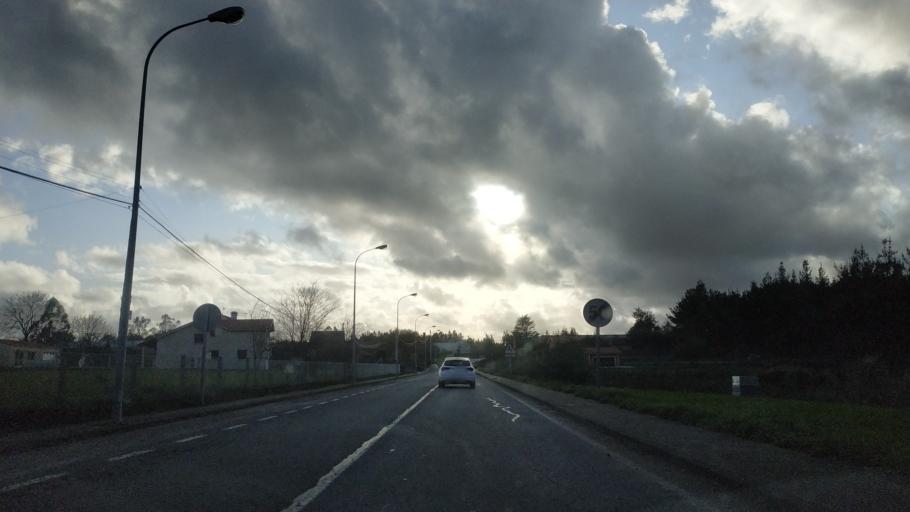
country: ES
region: Galicia
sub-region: Provincia da Coruna
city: Arzua
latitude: 42.9186
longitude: -8.1657
